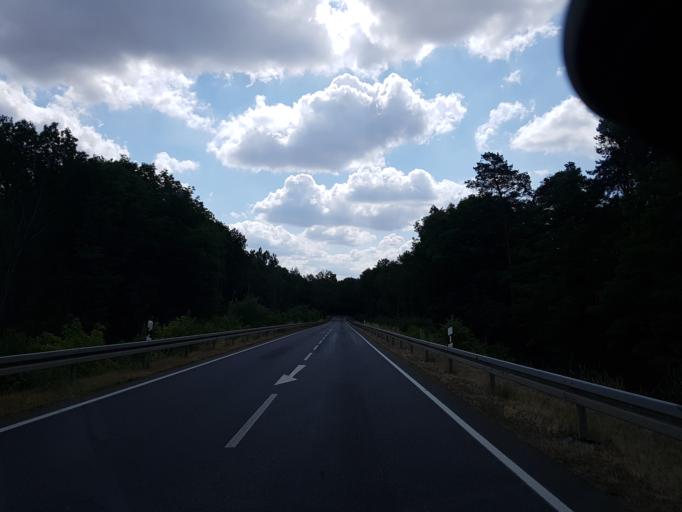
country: DE
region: Brandenburg
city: Drebkau
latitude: 51.6684
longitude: 14.1775
